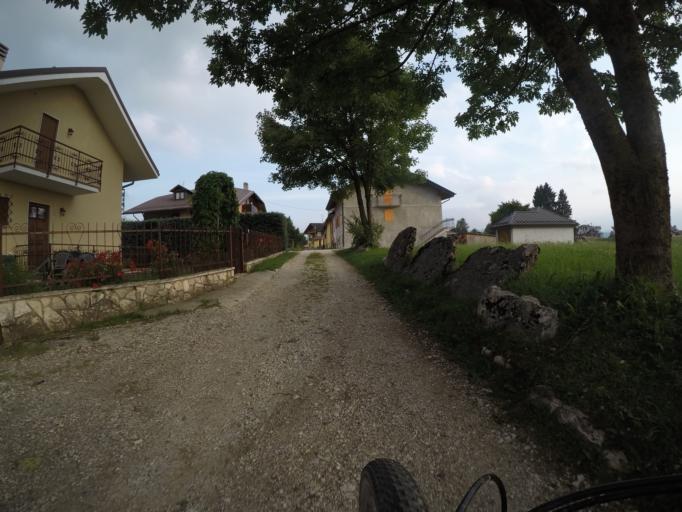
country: IT
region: Veneto
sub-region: Provincia di Vicenza
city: Gallio
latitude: 45.8726
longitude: 11.5339
